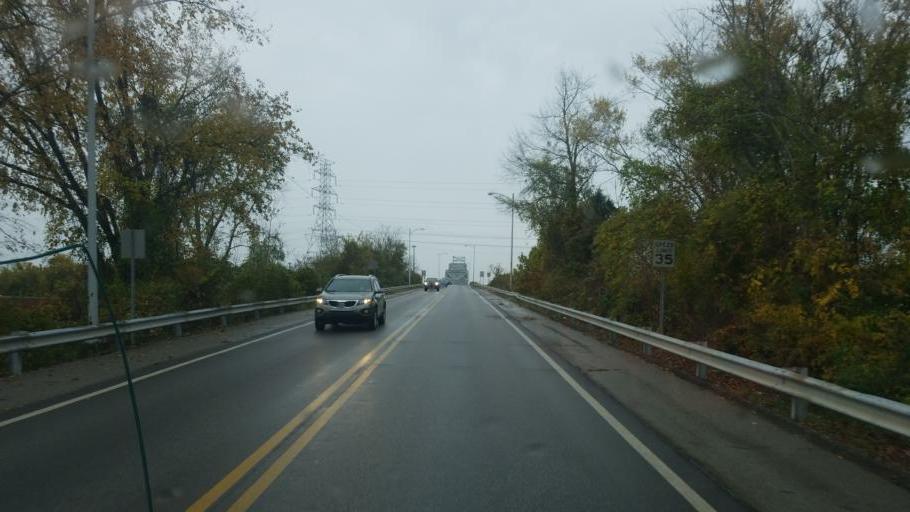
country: US
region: West Virginia
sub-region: Wood County
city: Parkersburg
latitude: 39.2830
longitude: -81.5560
